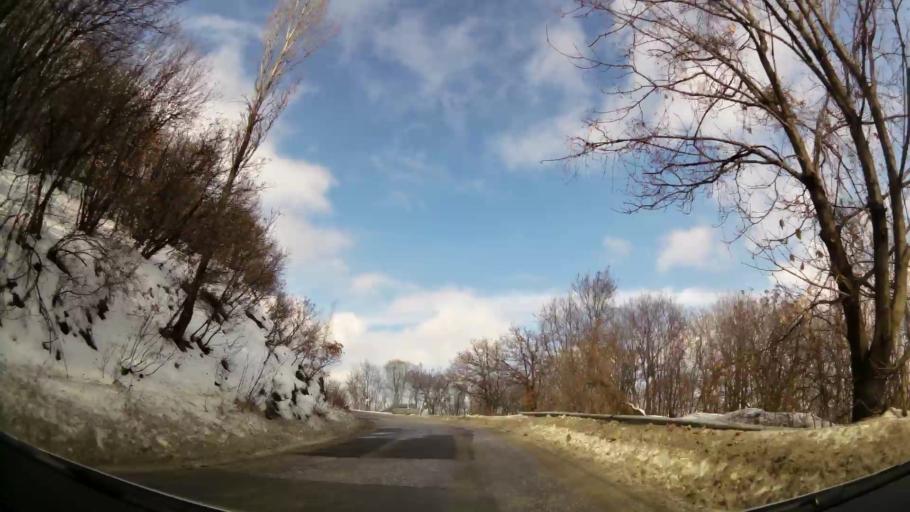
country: BG
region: Sofiya
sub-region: Obshtina Bozhurishte
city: Bozhurishte
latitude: 42.6430
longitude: 23.2263
